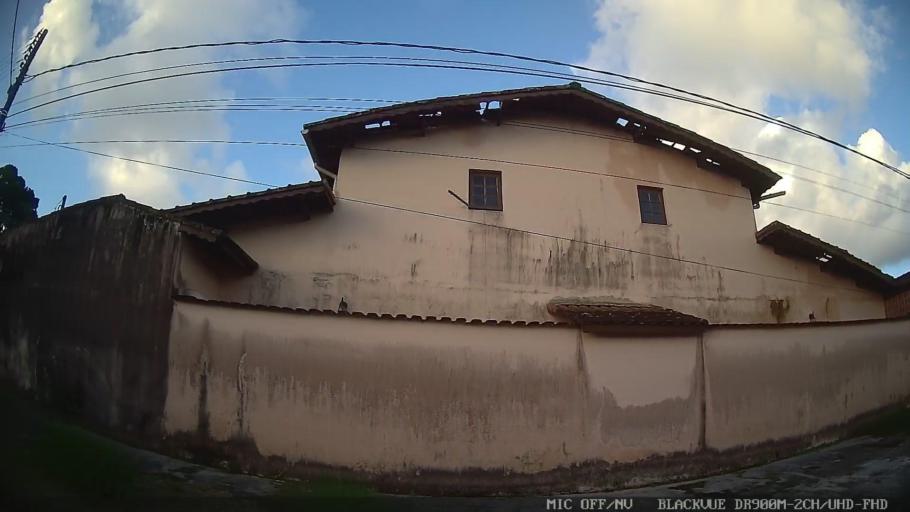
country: BR
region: Sao Paulo
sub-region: Itanhaem
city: Itanhaem
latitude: -24.1415
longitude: -46.7304
